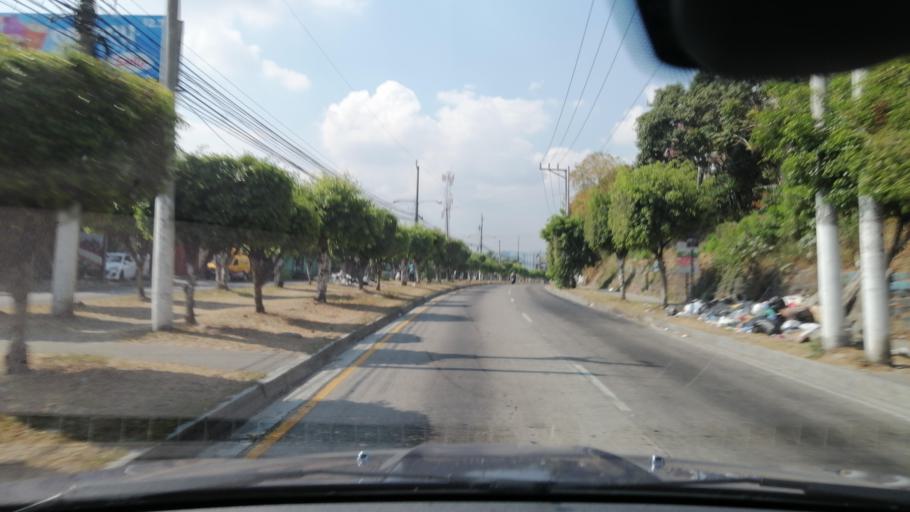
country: SV
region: San Salvador
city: Mejicanos
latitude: 13.7323
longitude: -89.2183
